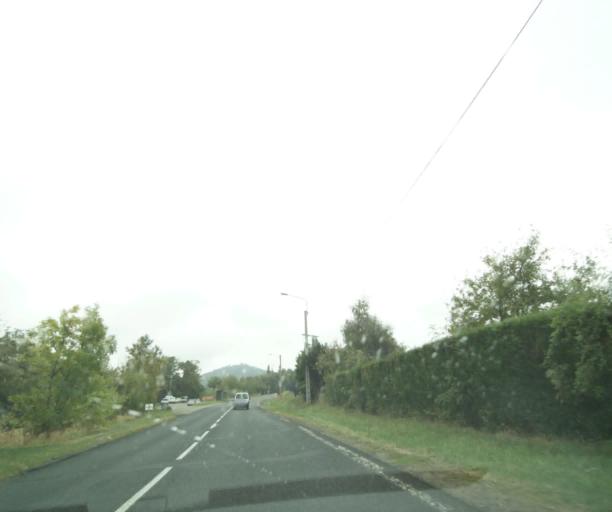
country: FR
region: Auvergne
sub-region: Departement du Puy-de-Dome
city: Ceyrat
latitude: 45.7221
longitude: 3.0676
